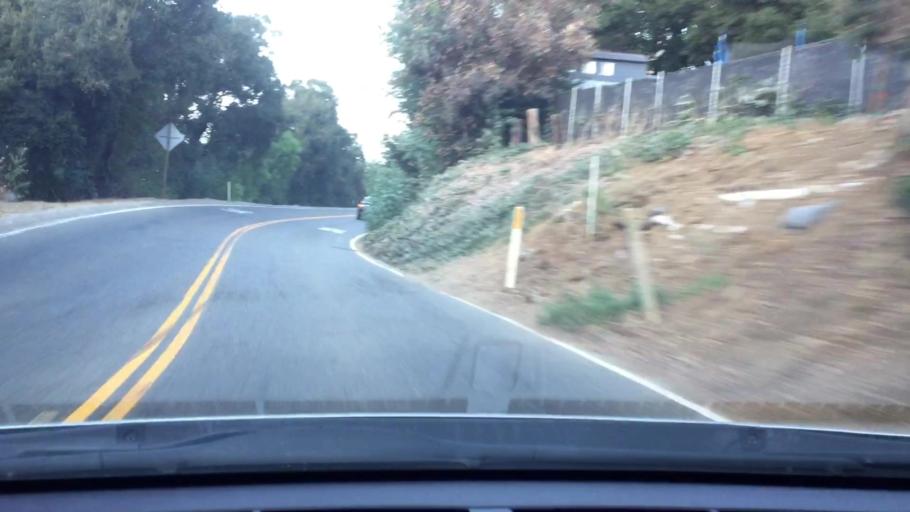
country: US
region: California
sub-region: San Bernardino County
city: Chino Hills
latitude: 33.9468
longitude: -117.7799
